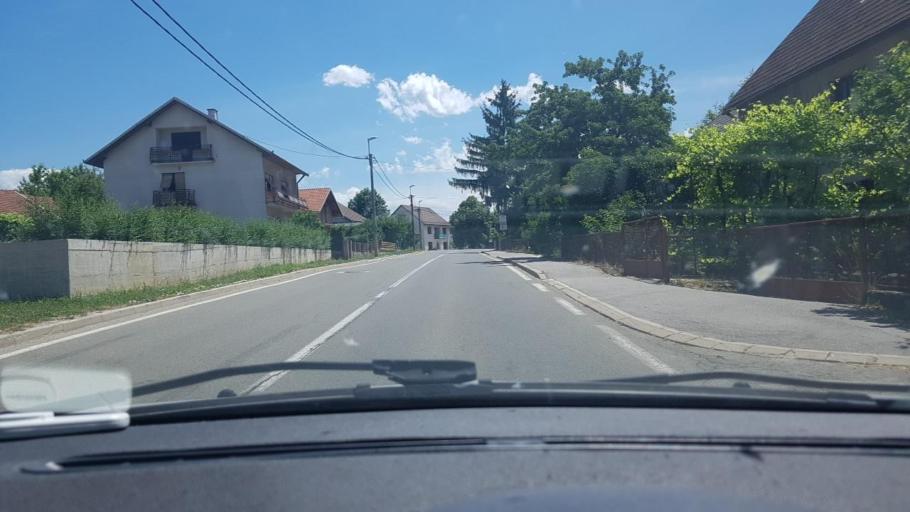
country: HR
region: Licko-Senjska
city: Otocac
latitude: 44.8663
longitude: 15.2557
